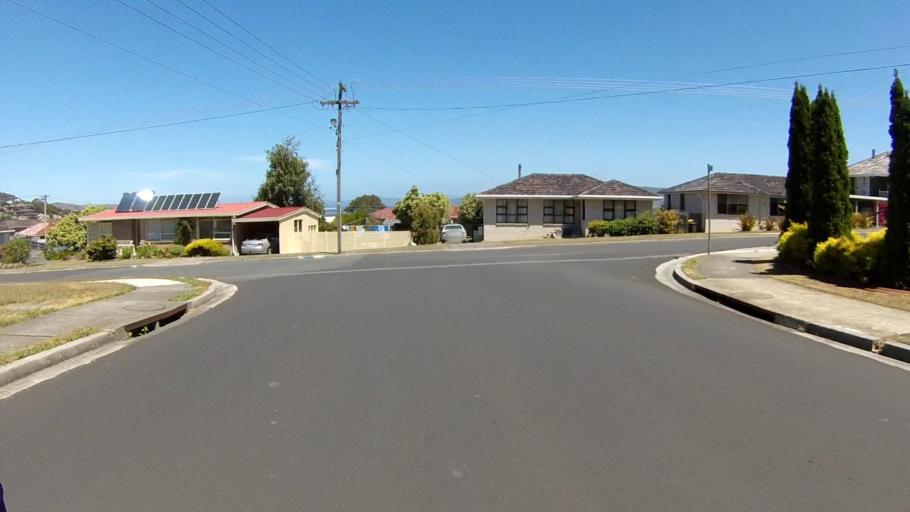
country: AU
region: Tasmania
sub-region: Clarence
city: Howrah
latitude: -42.8770
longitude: 147.4094
